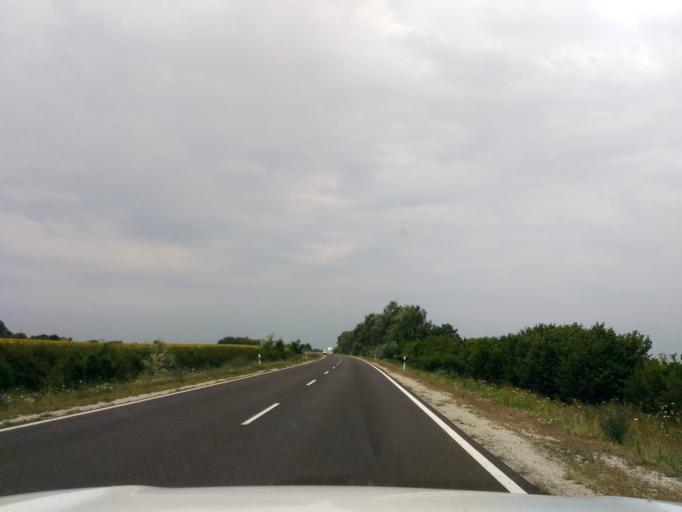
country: HU
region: Jasz-Nagykun-Szolnok
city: Zagyvarekas
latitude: 47.1894
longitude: 20.0930
